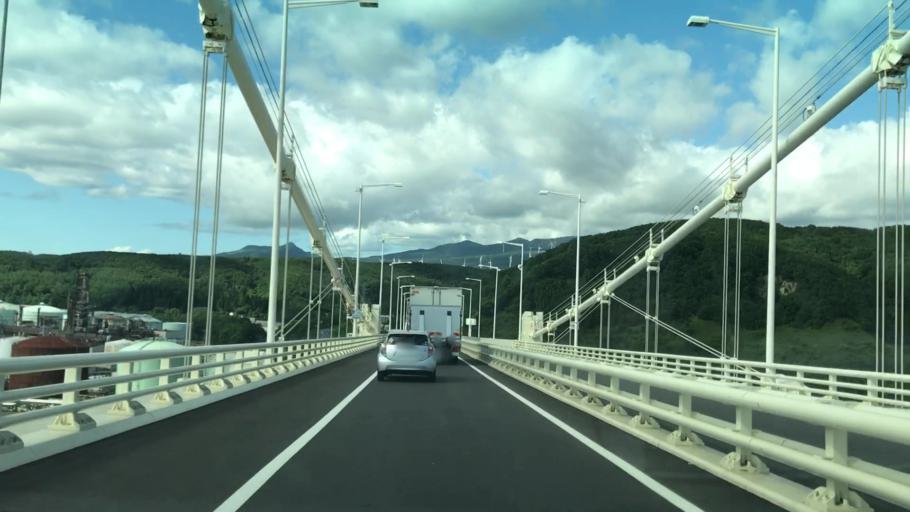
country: JP
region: Hokkaido
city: Muroran
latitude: 42.3583
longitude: 140.9510
